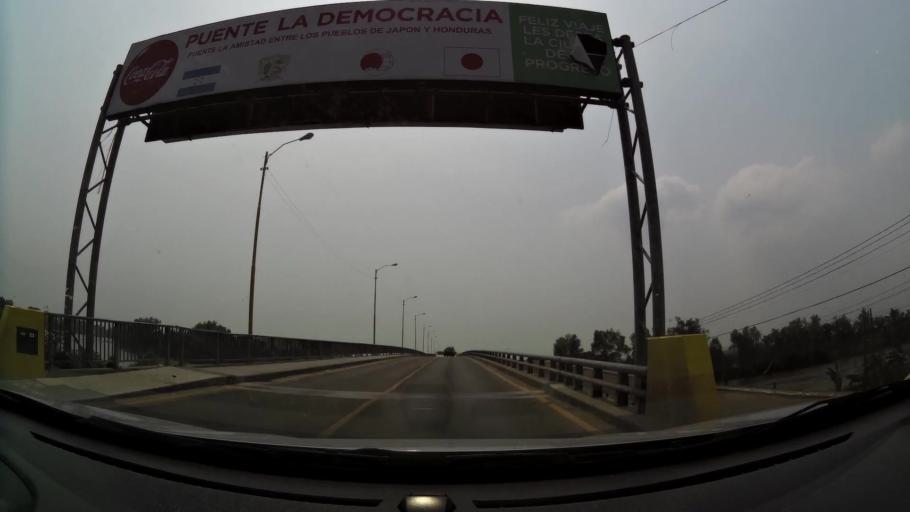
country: HN
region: Yoro
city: El Progreso
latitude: 15.4036
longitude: -87.8189
